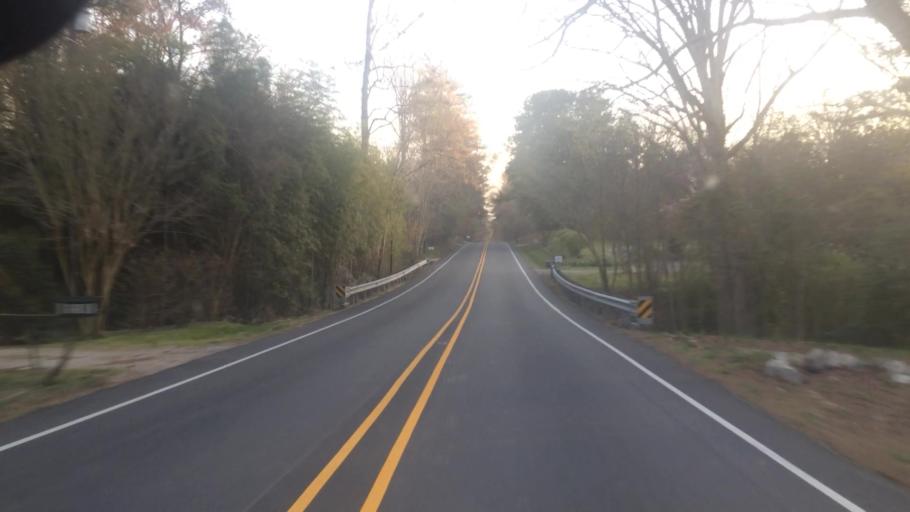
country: US
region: Virginia
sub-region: James City County
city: Williamsburg
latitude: 37.2429
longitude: -76.7425
